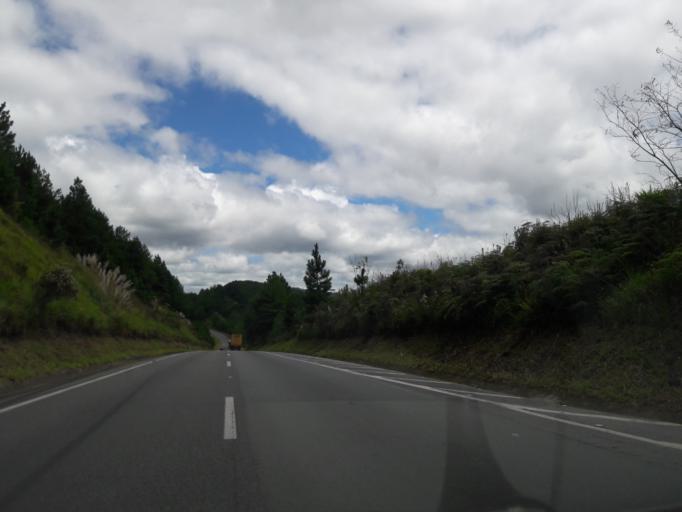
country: BR
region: Parana
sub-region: Campina Grande Do Sul
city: Campina Grande do Sul
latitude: -25.1052
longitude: -48.8416
